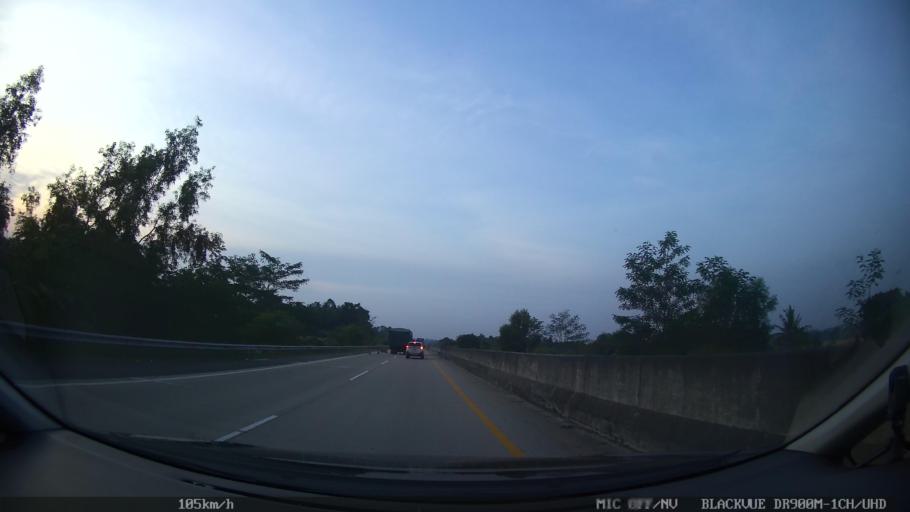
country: ID
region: Lampung
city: Penengahan
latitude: -5.7717
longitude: 105.7166
